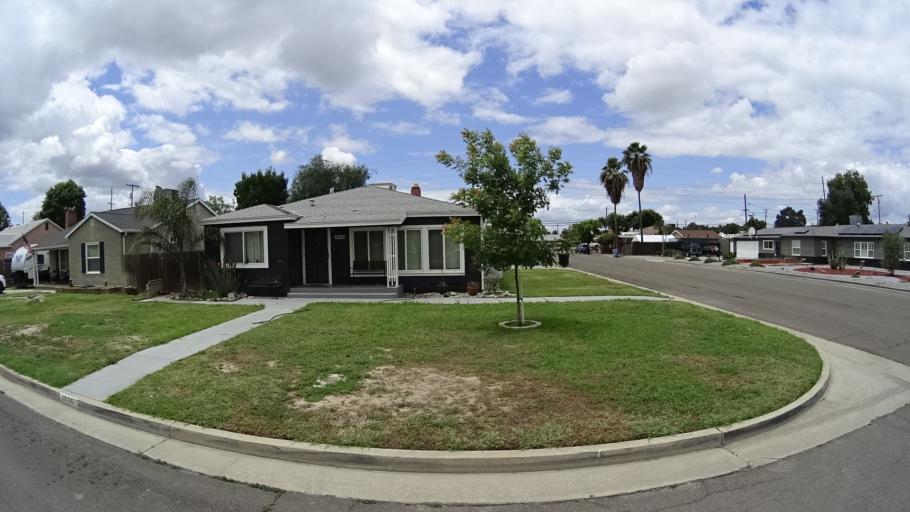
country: US
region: California
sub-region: Kings County
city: Hanford
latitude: 36.3462
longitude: -119.6540
